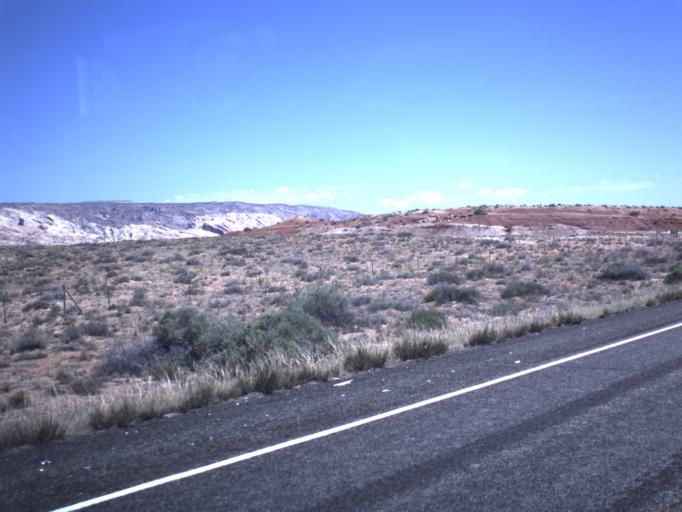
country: US
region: Utah
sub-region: Emery County
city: Castle Dale
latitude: 38.7197
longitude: -110.4918
